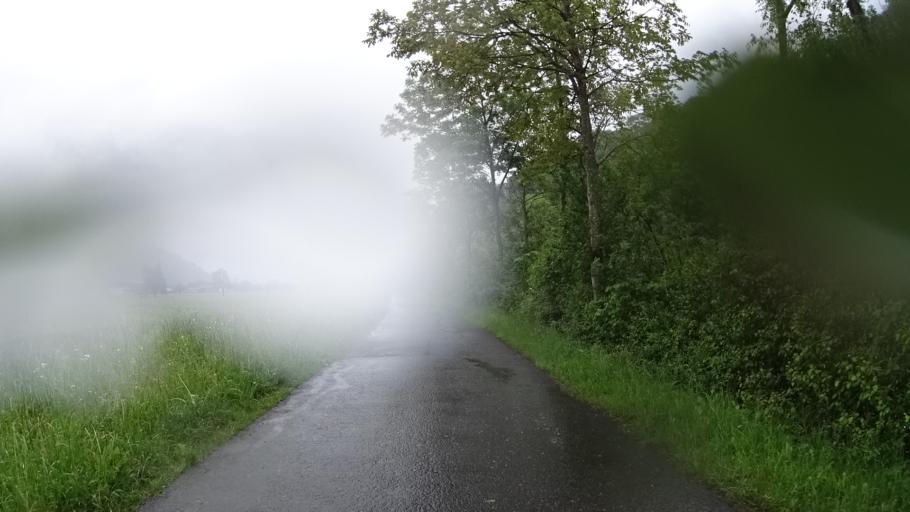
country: CH
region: Saint Gallen
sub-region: Wahlkreis Sarganserland
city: Sargans
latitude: 47.0608
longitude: 9.3948
